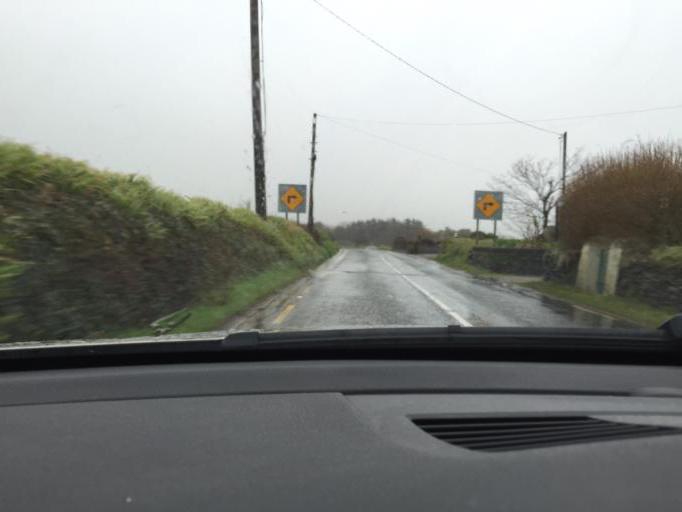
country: IE
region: Munster
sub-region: Ciarrai
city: Dingle
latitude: 52.1254
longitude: -10.3233
